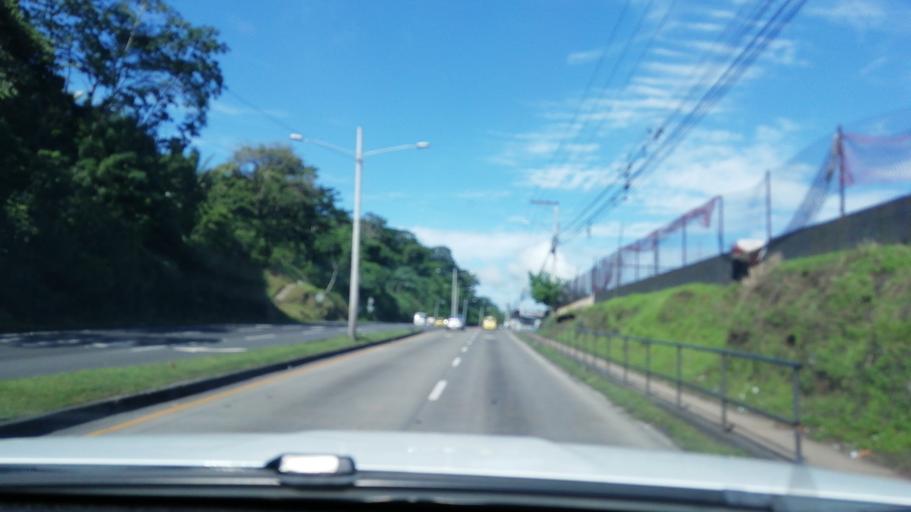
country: PA
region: Panama
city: Alcalde Diaz
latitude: 9.1099
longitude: -79.5513
